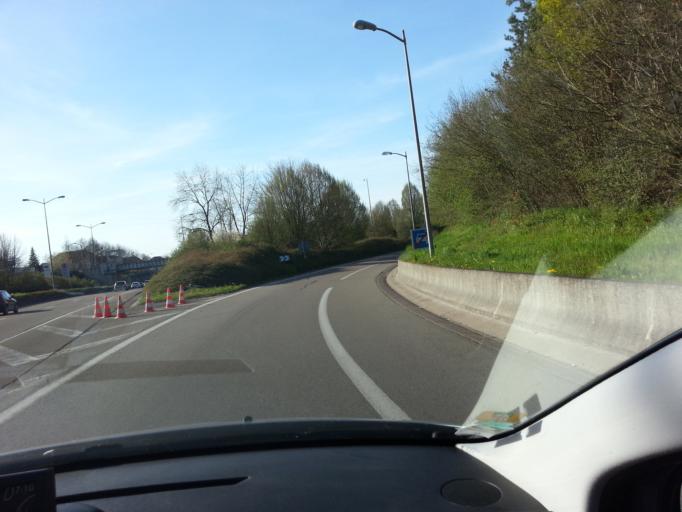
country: FR
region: Franche-Comte
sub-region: Departement du Doubs
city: Besancon
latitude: 47.2707
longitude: 6.0000
